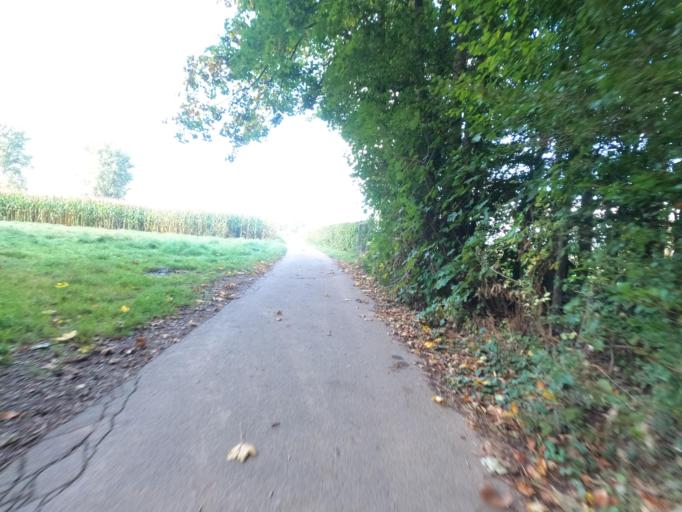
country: DE
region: North Rhine-Westphalia
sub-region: Regierungsbezirk Koln
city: Linnich
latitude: 50.9577
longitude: 6.3045
